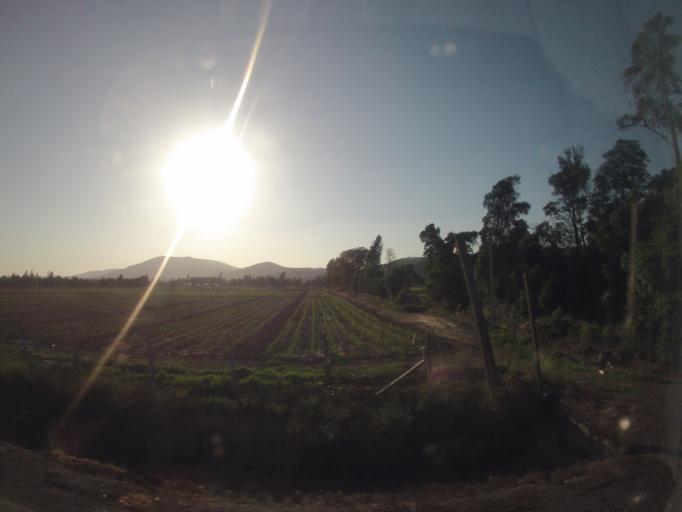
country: CL
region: O'Higgins
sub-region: Provincia de Colchagua
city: Chimbarongo
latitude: -34.6539
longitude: -70.9926
